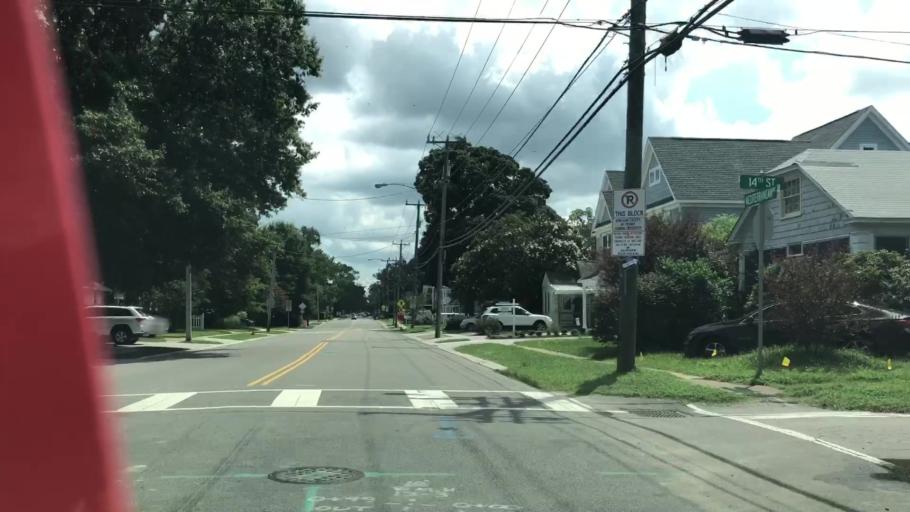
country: US
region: Virginia
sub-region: City of Virginia Beach
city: Virginia Beach
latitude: 36.8414
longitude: -75.9804
